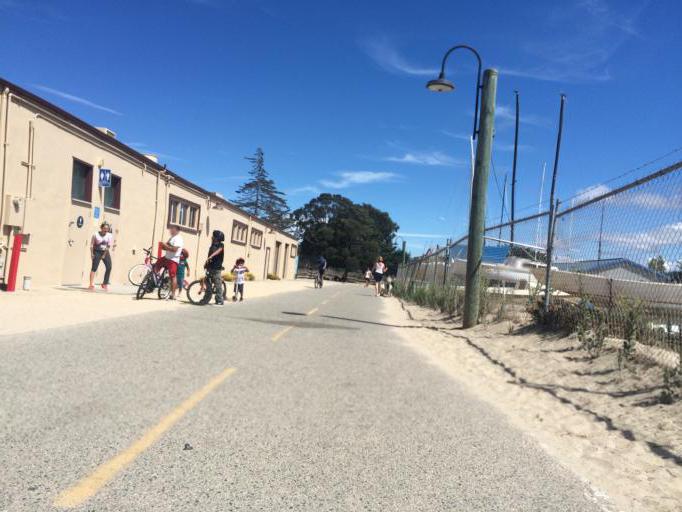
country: US
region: California
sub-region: Monterey County
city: Monterey
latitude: 36.6010
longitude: -121.8893
